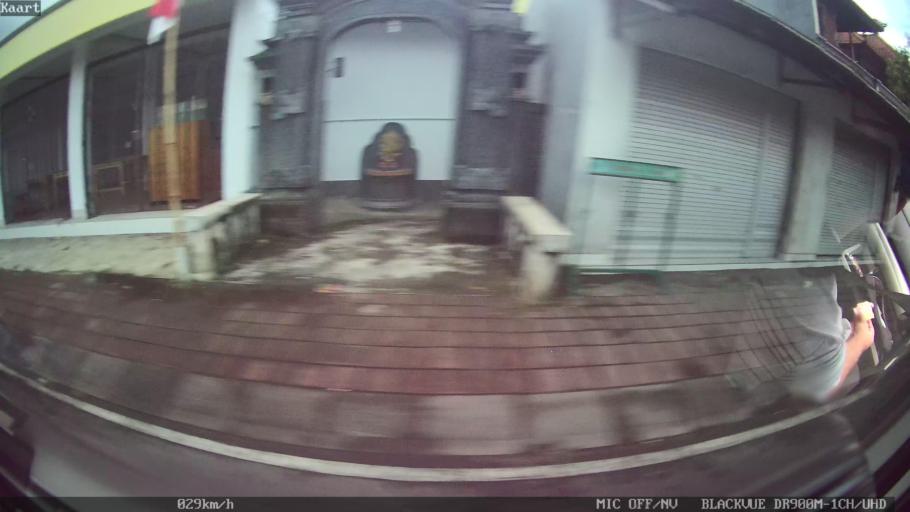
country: ID
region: Bali
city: Banjar Cemenggon
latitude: -8.5343
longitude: 115.2000
